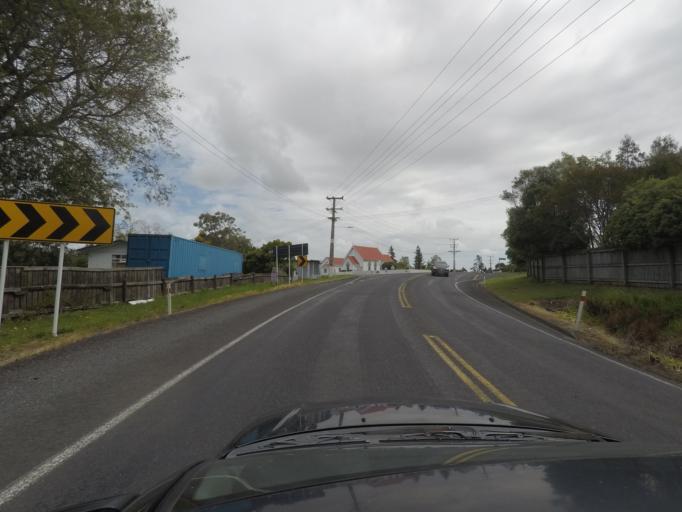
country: NZ
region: Auckland
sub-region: Auckland
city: Parakai
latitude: -36.6261
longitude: 174.5019
